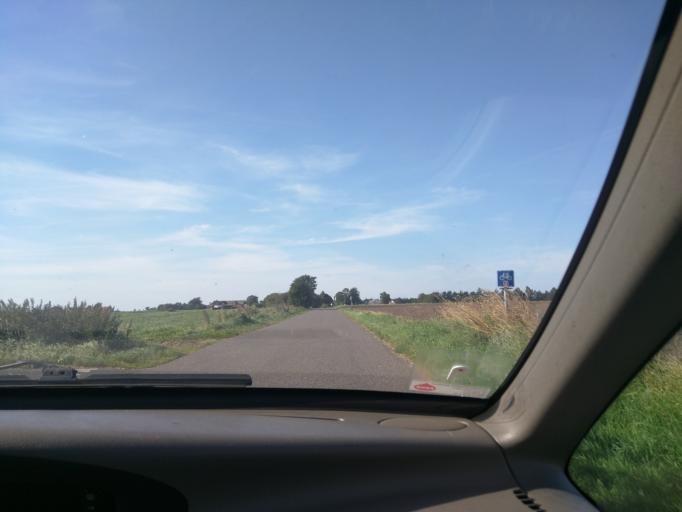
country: DK
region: Central Jutland
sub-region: Viborg Kommune
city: Bjerringbro
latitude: 56.4763
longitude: 9.6081
